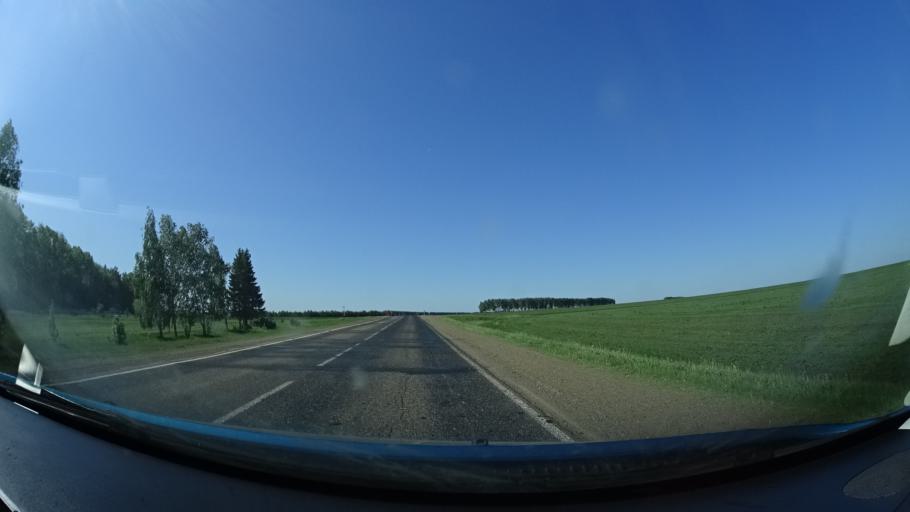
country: RU
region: Bashkortostan
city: Starobaltachevo
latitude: 55.9225
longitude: 55.7845
